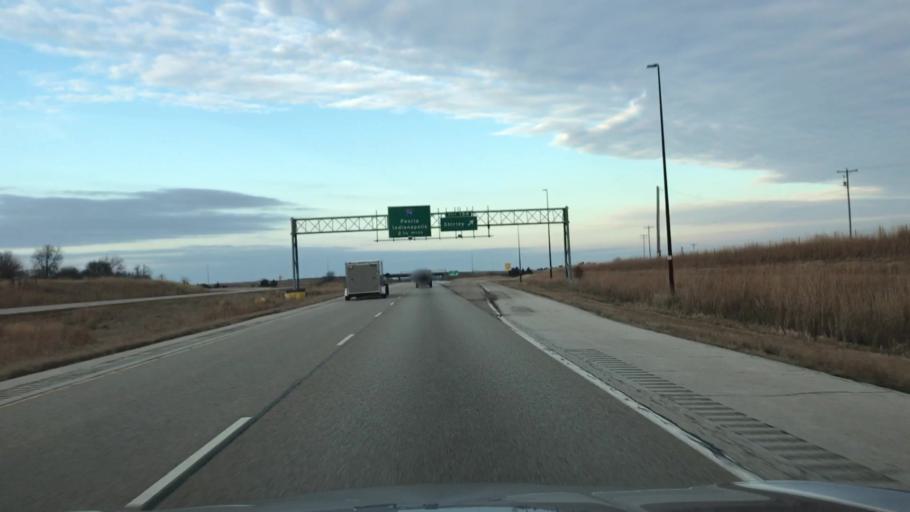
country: US
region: Illinois
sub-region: McLean County
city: Twin Grove
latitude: 40.4033
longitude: -89.0568
